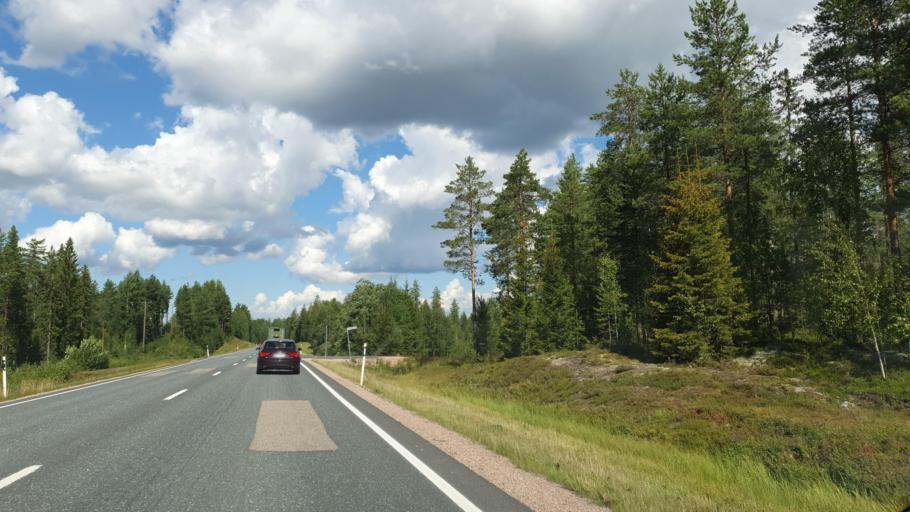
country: FI
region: Kainuu
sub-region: Kajaani
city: Kajaani
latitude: 64.1030
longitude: 27.4491
